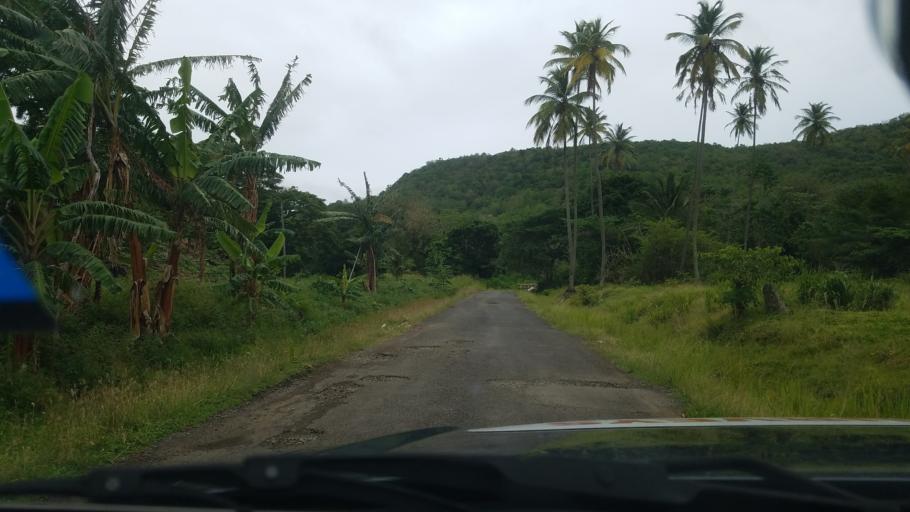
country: LC
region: Castries Quarter
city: Bisee
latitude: 14.0118
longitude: -60.9180
